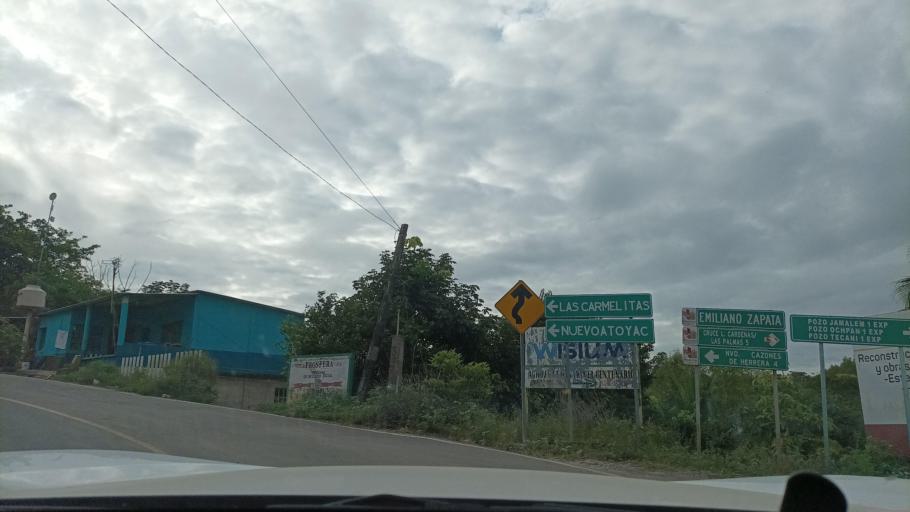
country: MX
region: Veracruz
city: Hidalgotitlan
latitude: 17.6867
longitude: -94.4690
